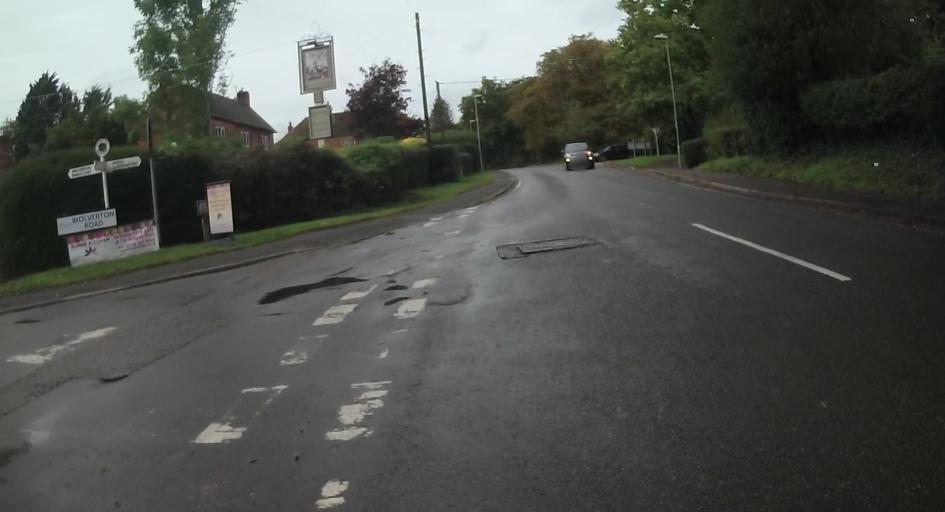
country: GB
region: England
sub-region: Hampshire
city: Tadley
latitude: 51.3527
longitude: -1.1686
